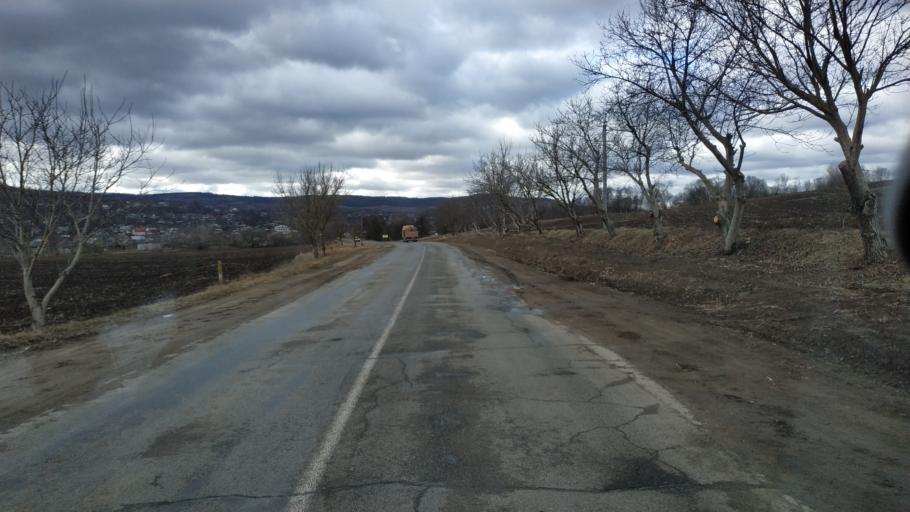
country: MD
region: Stinga Nistrului
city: Bucovat
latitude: 47.1662
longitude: 28.4371
